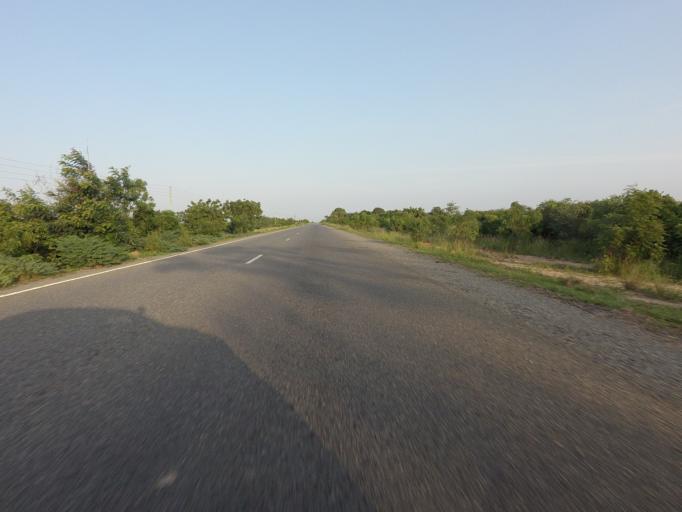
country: GH
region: Volta
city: Anloga
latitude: 5.8899
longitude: 0.7200
